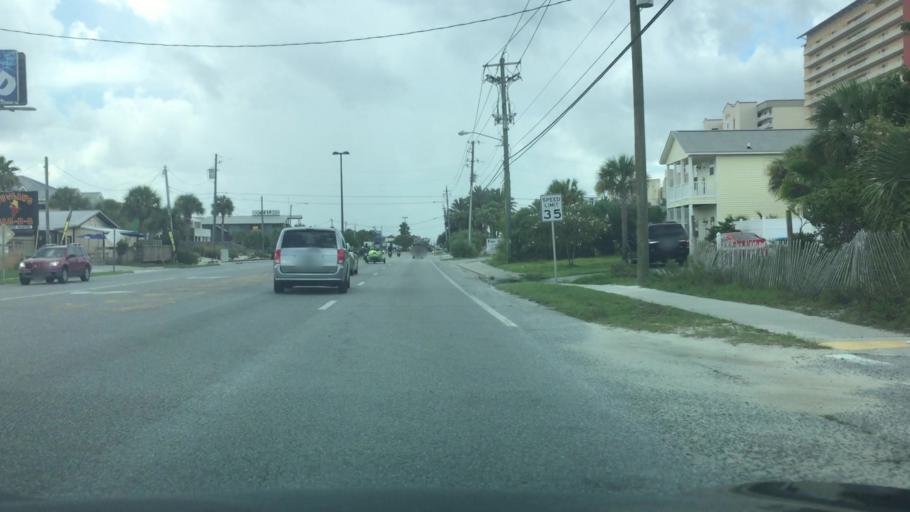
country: US
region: Florida
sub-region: Bay County
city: Lower Grand Lagoon
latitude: 30.1553
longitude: -85.7707
